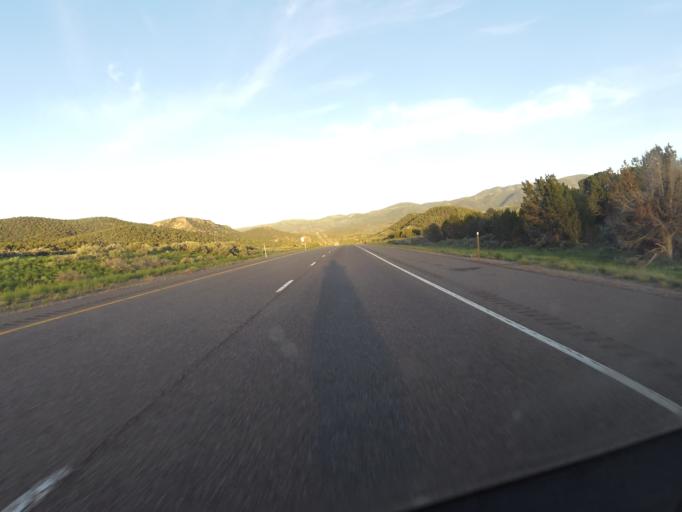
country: US
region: Utah
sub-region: Sevier County
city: Monroe
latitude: 38.5718
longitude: -112.4547
